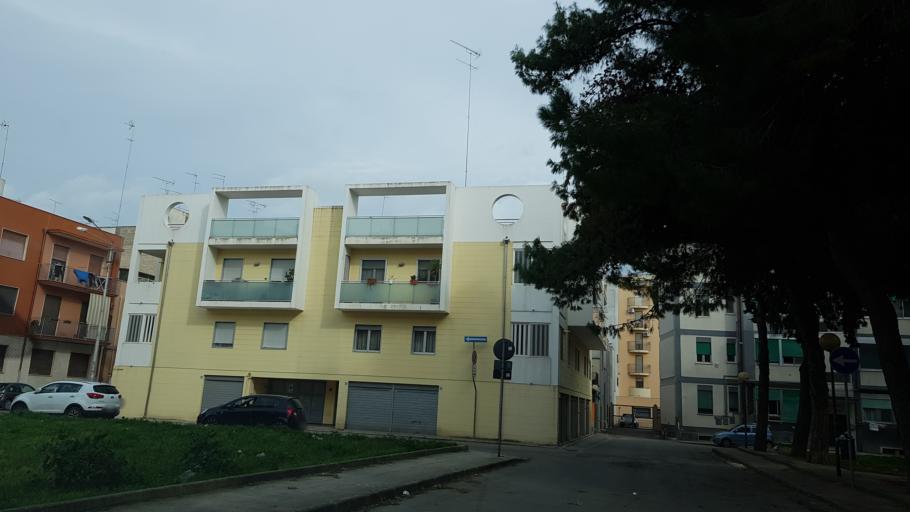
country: IT
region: Apulia
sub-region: Provincia di Brindisi
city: Brindisi
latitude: 40.6289
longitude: 17.9302
